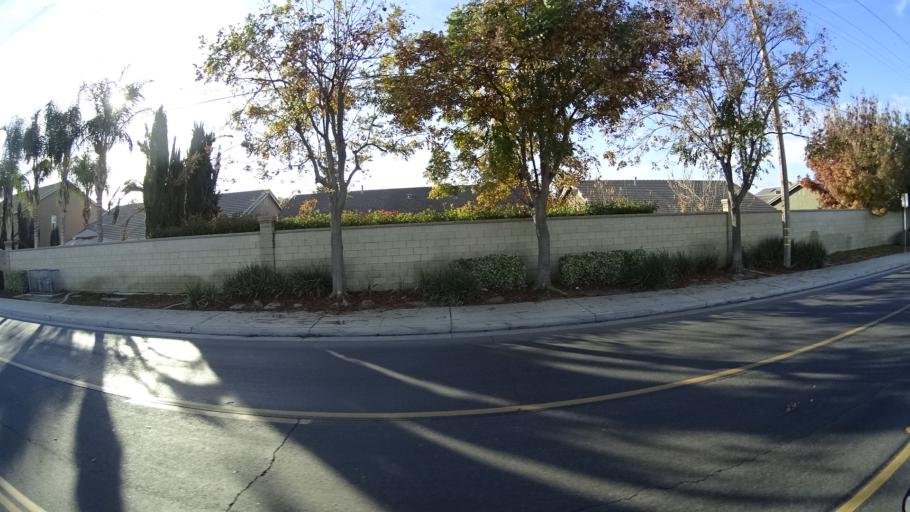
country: US
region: California
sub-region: Kern County
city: Rosedale
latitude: 35.3035
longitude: -119.1357
